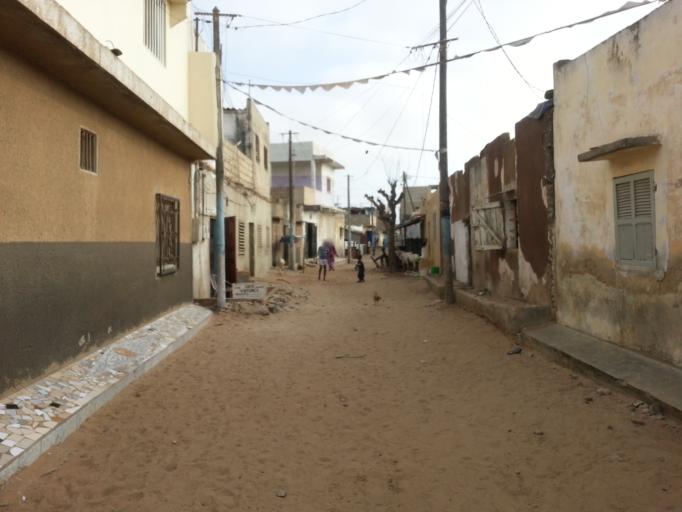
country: SN
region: Dakar
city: Pikine
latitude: 14.7700
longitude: -17.3858
